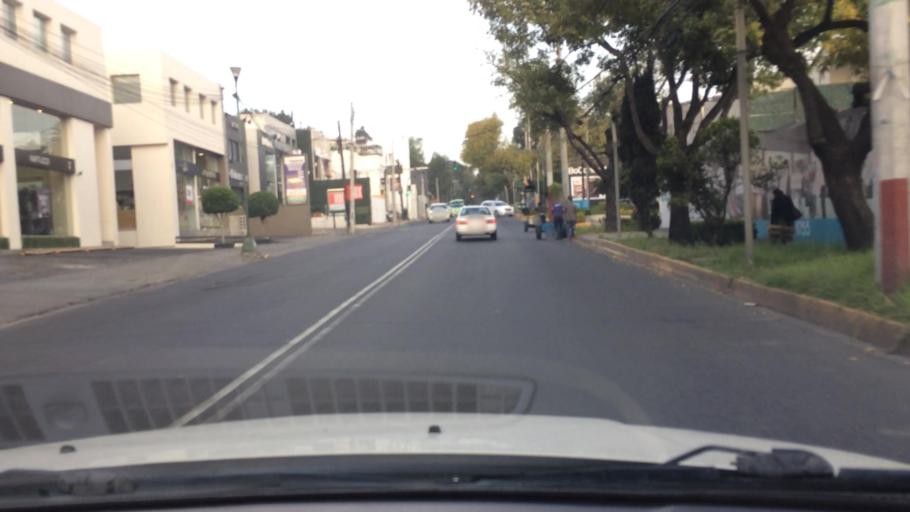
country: MX
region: Mexico City
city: Alvaro Obregon
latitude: 19.3484
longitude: -99.1926
